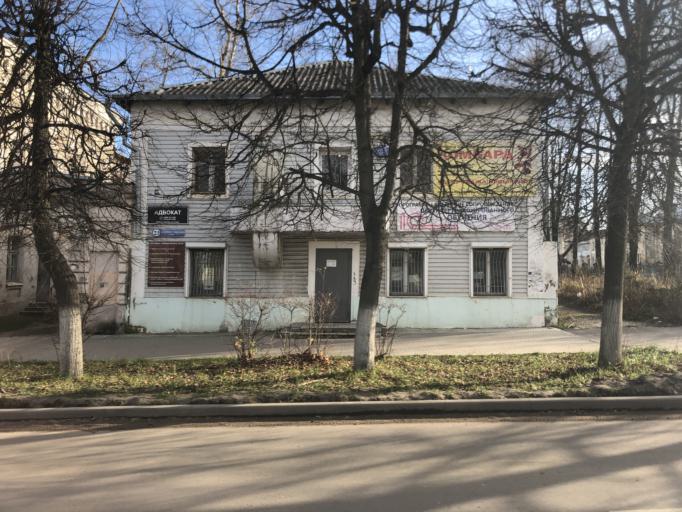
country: RU
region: Tverskaya
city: Rzhev
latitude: 56.2554
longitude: 34.3281
